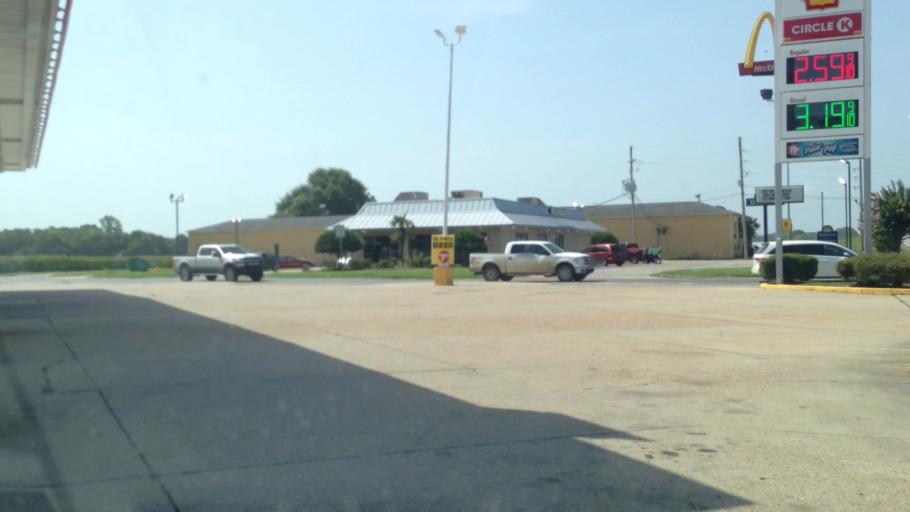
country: US
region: Louisiana
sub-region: Madison Parish
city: Tallulah
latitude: 32.3966
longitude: -91.1991
